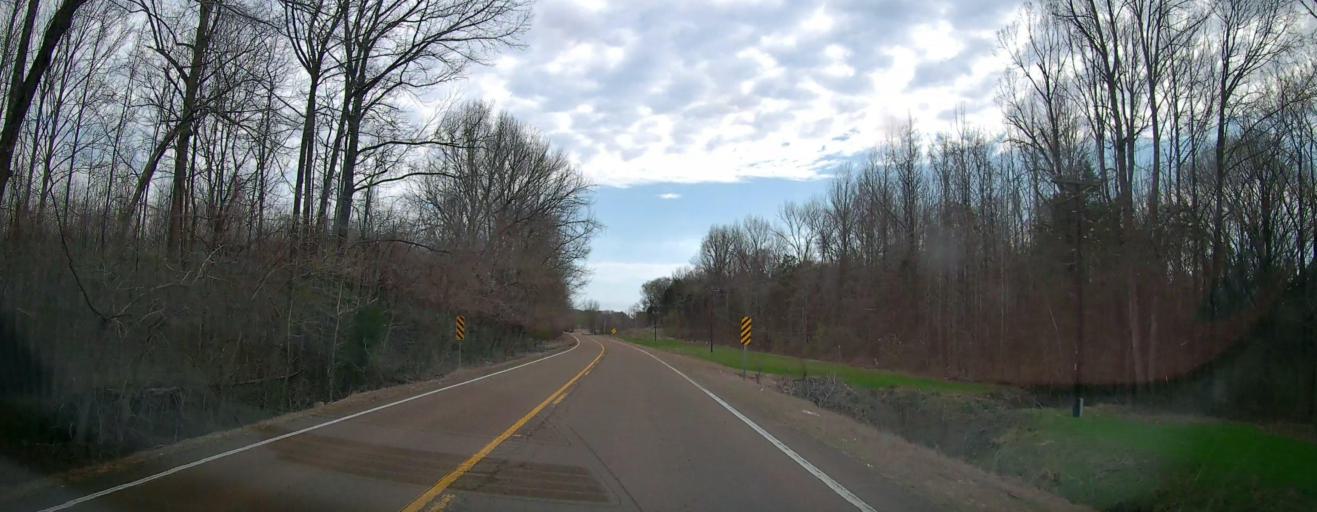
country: US
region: Mississippi
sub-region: Marshall County
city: Byhalia
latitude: 34.8486
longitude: -89.6269
